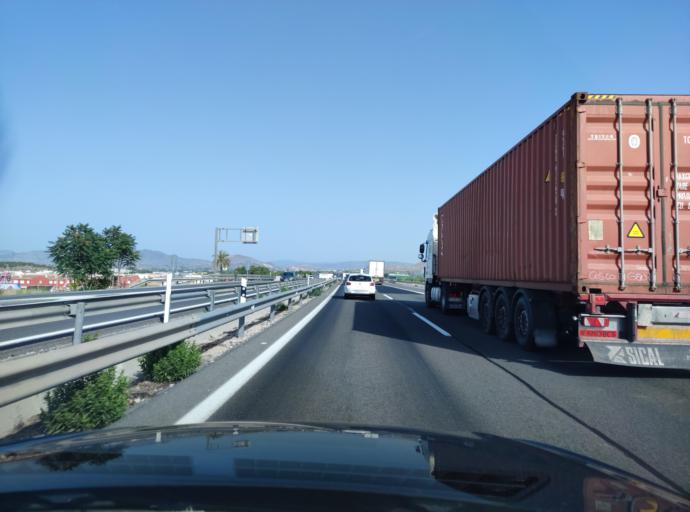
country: ES
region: Valencia
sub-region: Provincia de Alicante
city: Monforte del Cid
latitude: 38.3841
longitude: -0.7217
